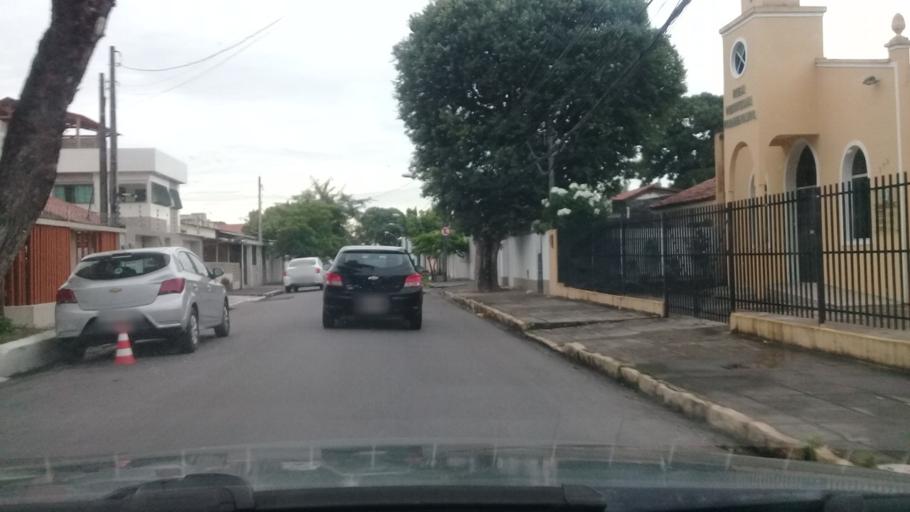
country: BR
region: Pernambuco
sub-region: Recife
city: Recife
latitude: -8.1119
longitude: -34.9251
